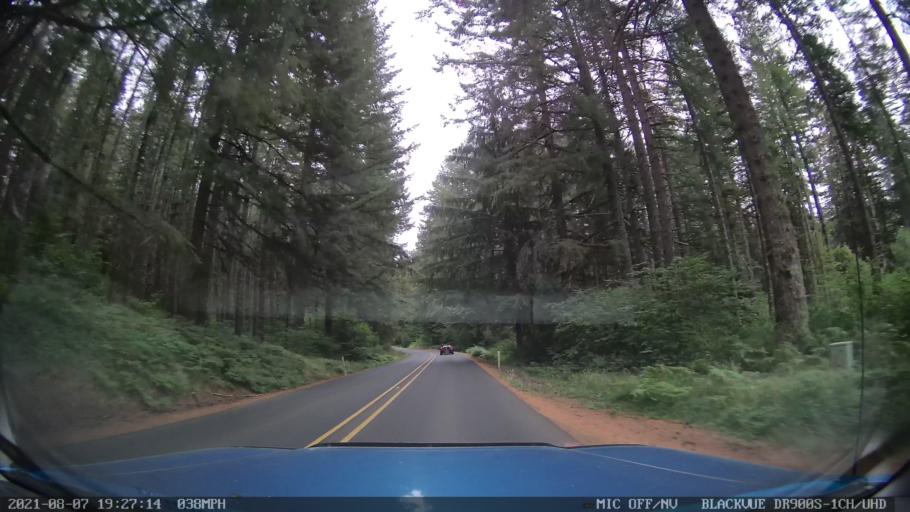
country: US
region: Oregon
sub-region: Linn County
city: Lyons
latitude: 44.8780
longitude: -122.6486
